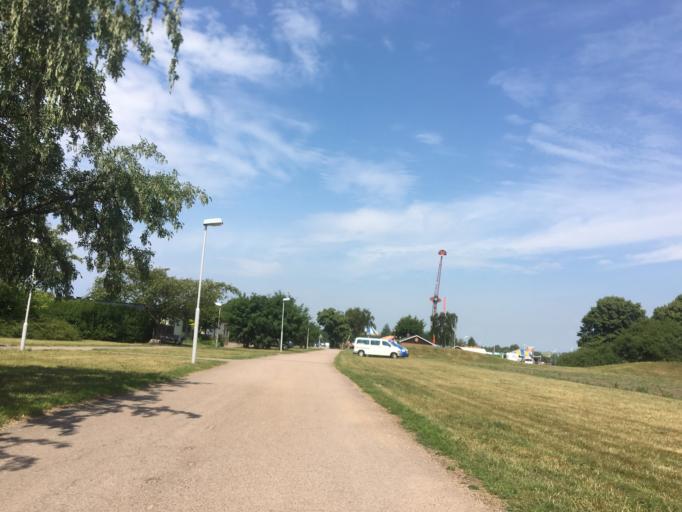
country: SE
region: Skane
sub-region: Landskrona
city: Landskrona
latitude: 55.8955
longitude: 12.8133
